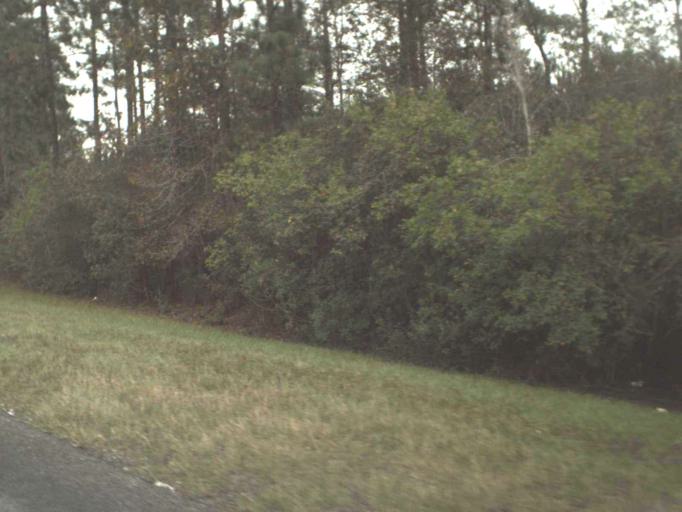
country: US
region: Florida
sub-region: Escambia County
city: Molino
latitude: 30.7854
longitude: -87.3348
